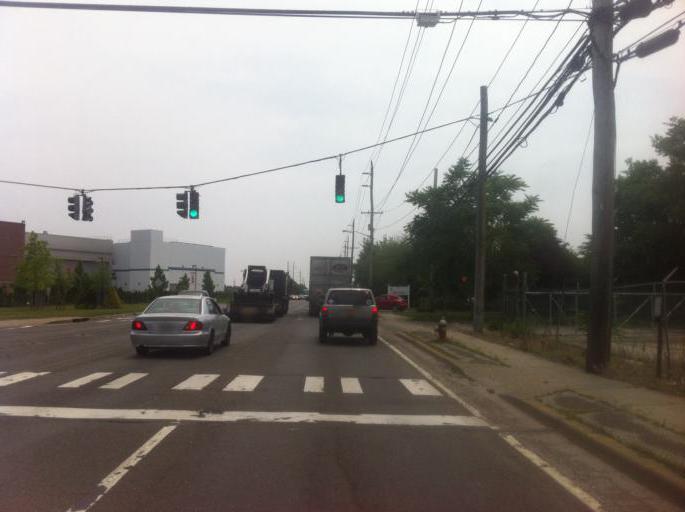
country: US
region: New York
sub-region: Nassau County
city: Bethpage
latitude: 40.7487
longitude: -73.5030
